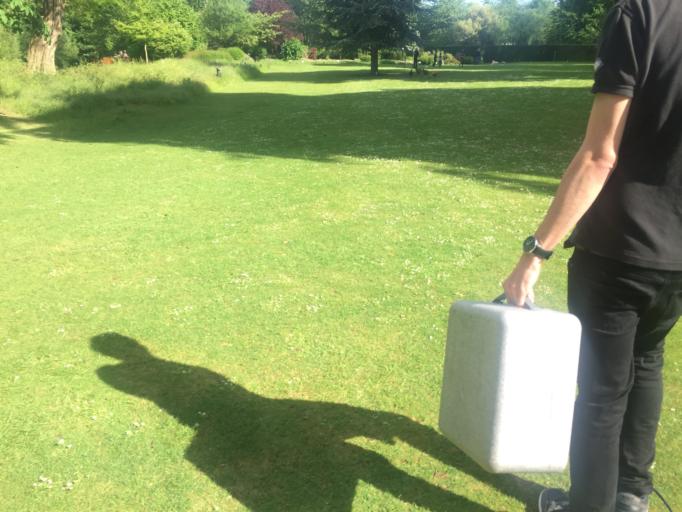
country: GB
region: England
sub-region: Royal Borough of Windsor and Maidenhead
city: Cookham
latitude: 51.5601
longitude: -0.7043
